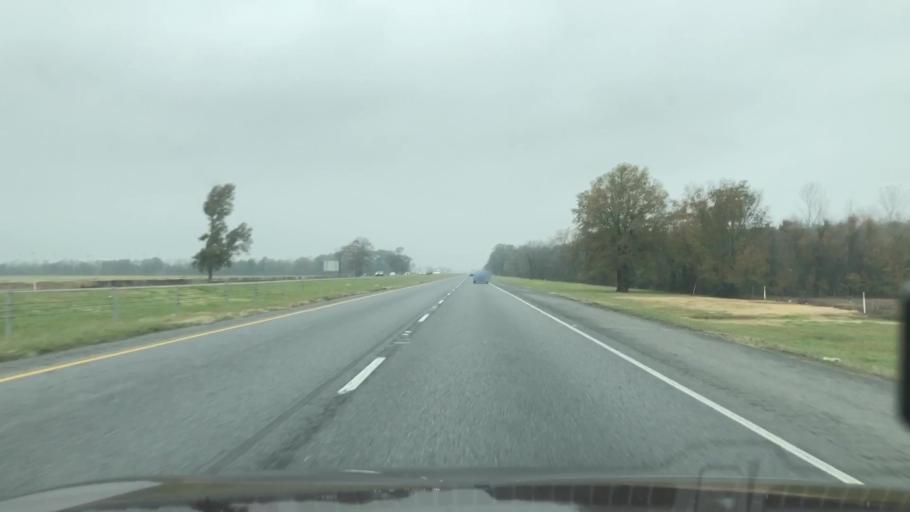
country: US
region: Louisiana
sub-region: Ouachita Parish
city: Lakeshore
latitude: 32.4903
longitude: -92.0044
